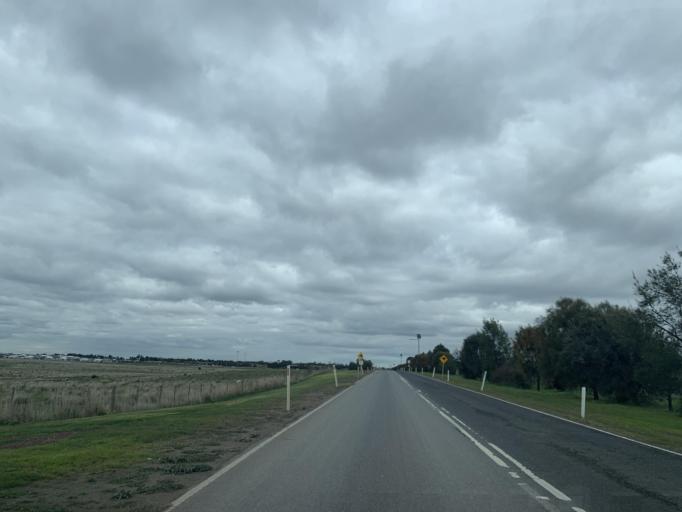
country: AU
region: Victoria
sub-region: Hume
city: Craigieburn
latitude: -37.5933
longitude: 144.9743
